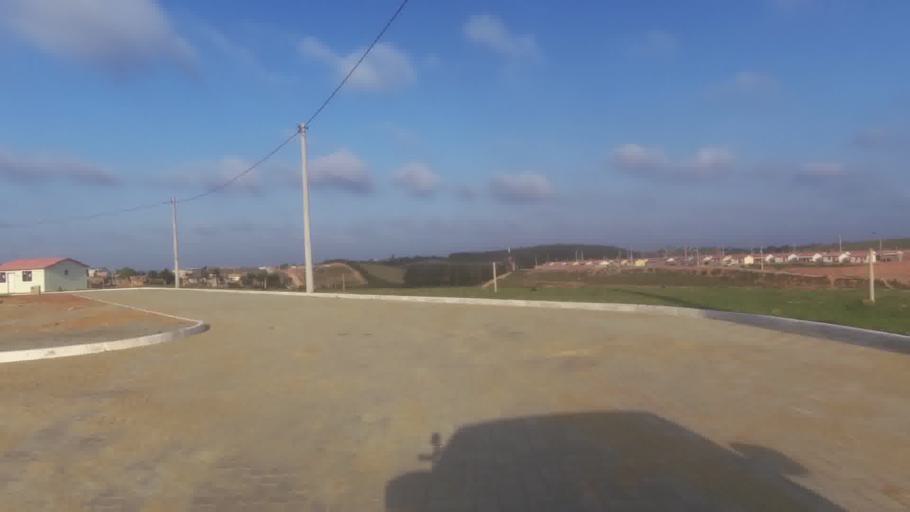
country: BR
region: Espirito Santo
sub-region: Itapemirim
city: Itapemirim
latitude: -21.0165
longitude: -40.8332
